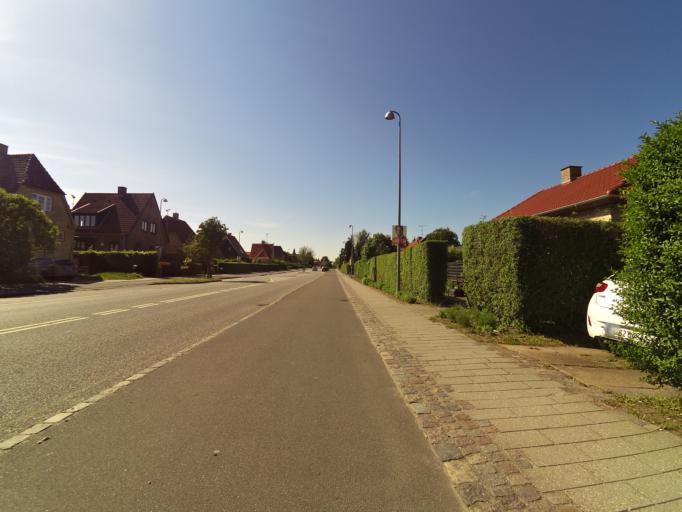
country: DK
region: Capital Region
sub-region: Gladsaxe Municipality
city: Buddinge
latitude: 55.7636
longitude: 12.4928
